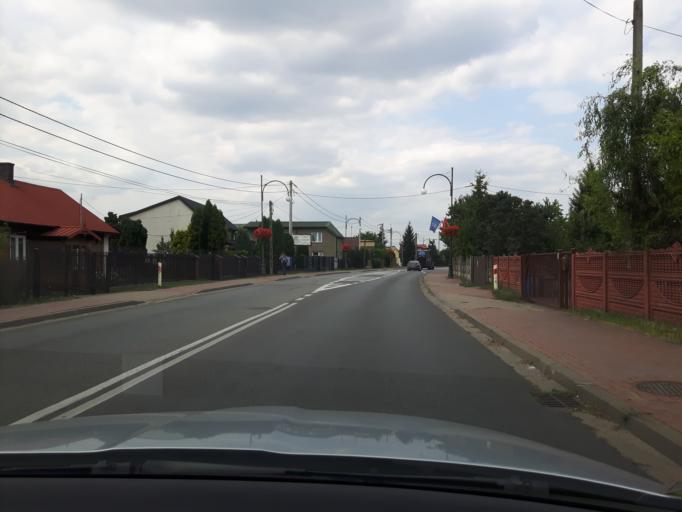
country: PL
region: Masovian Voivodeship
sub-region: Powiat legionowski
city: Nieporet
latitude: 52.4289
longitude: 21.0307
